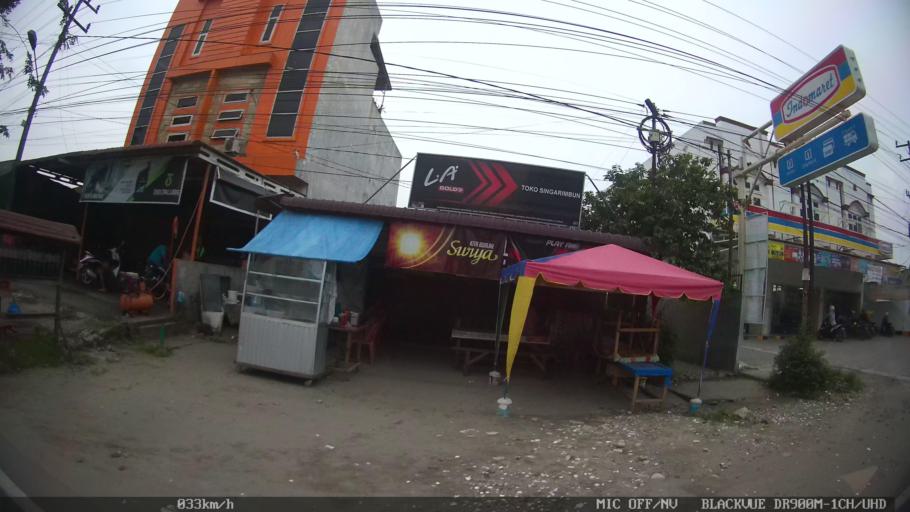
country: ID
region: North Sumatra
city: Deli Tua
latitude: 3.5495
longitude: 98.7154
